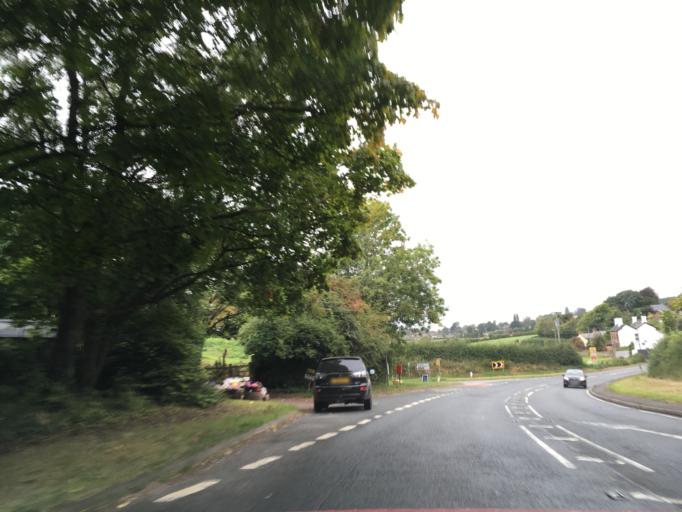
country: GB
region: England
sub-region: Herefordshire
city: Lea
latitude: 51.8987
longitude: -2.5224
